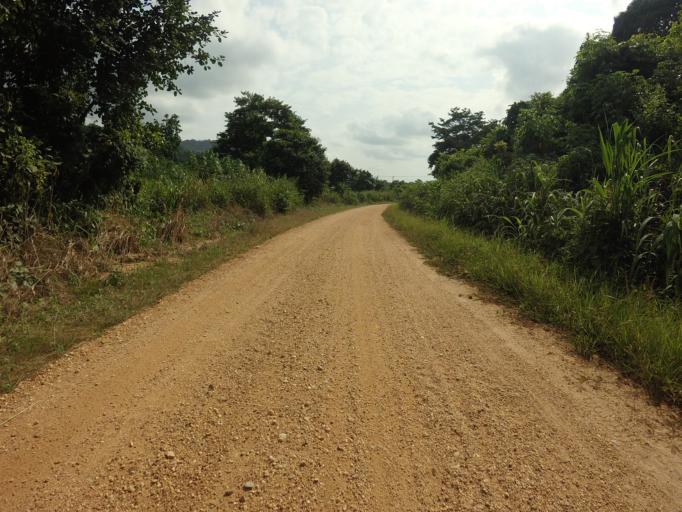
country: GH
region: Volta
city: Kpandu
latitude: 6.8724
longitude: 0.4272
